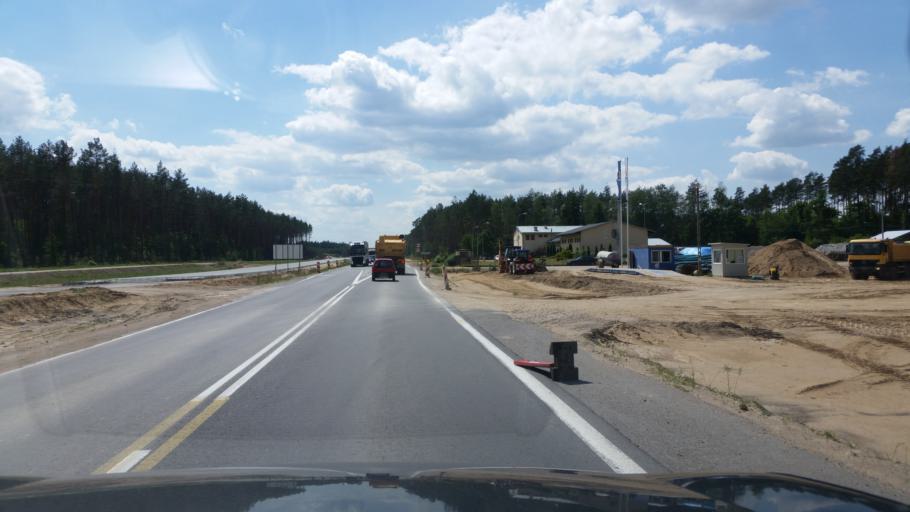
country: PL
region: Masovian Voivodeship
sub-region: Powiat ostrowski
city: Ostrow Mazowiecka
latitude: 52.7761
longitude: 21.8394
